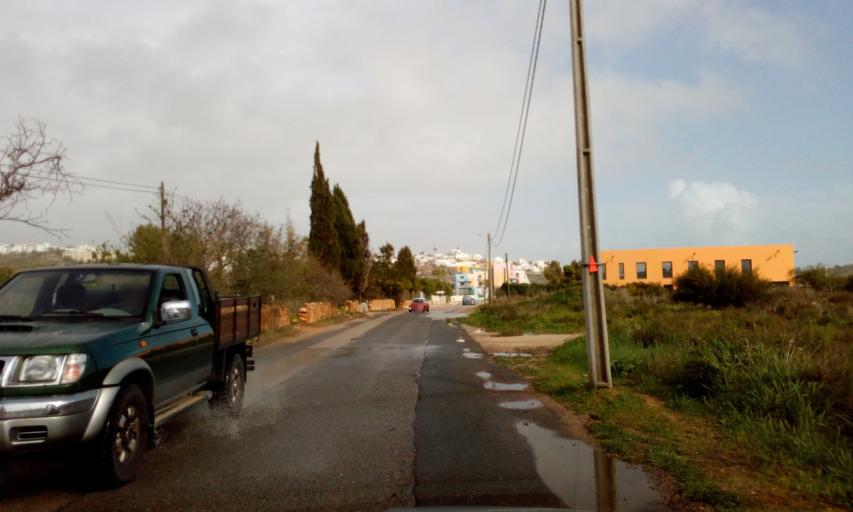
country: PT
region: Faro
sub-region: Albufeira
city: Albufeira
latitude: 37.0851
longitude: -8.2724
